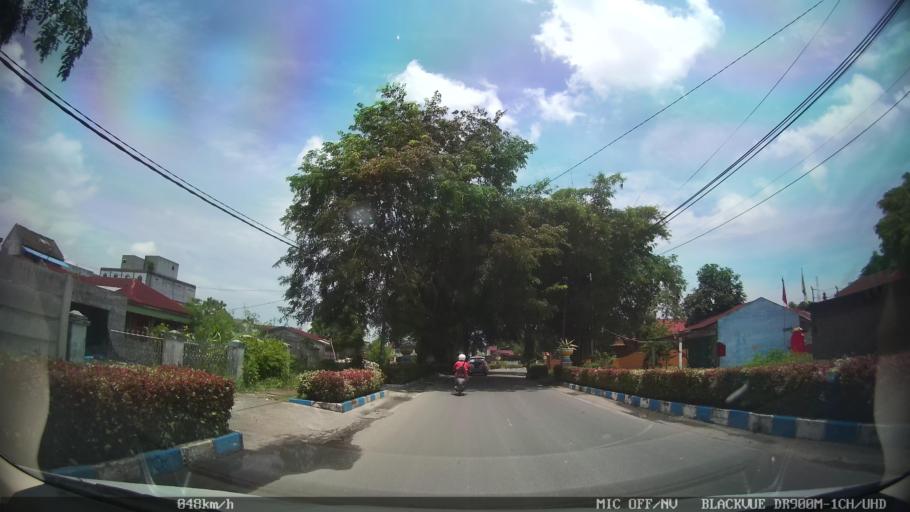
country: ID
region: North Sumatra
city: Percut
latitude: 3.5541
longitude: 98.8568
